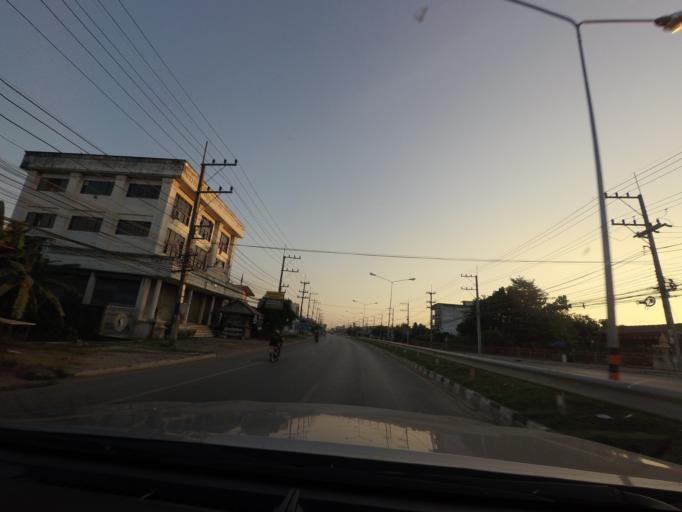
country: TH
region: Sukhothai
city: Sukhothai
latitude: 17.0253
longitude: 99.8223
